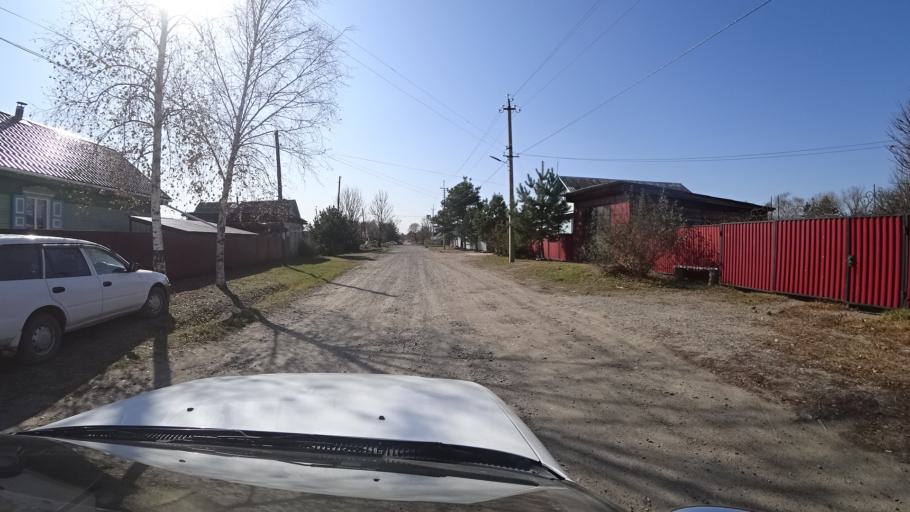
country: RU
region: Primorskiy
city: Dal'nerechensk
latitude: 45.9272
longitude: 133.7410
